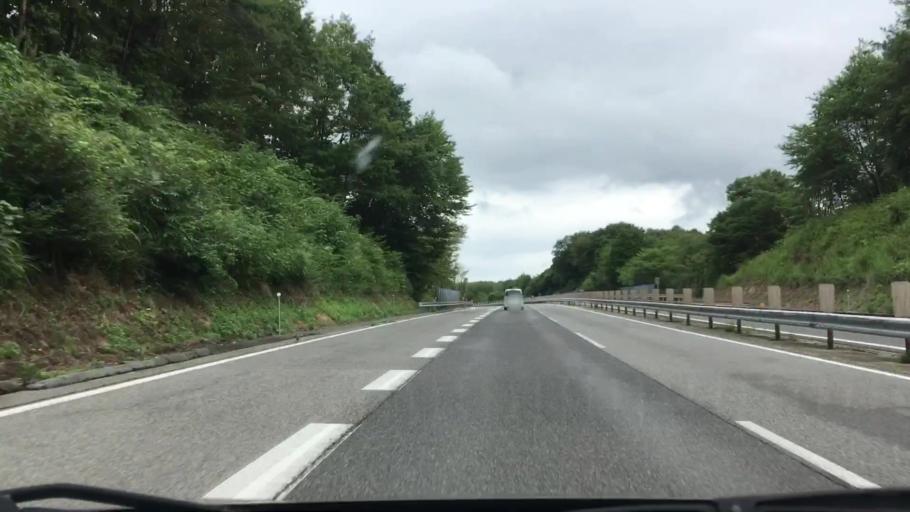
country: JP
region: Hiroshima
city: Miyoshi
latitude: 34.7545
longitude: 132.7601
